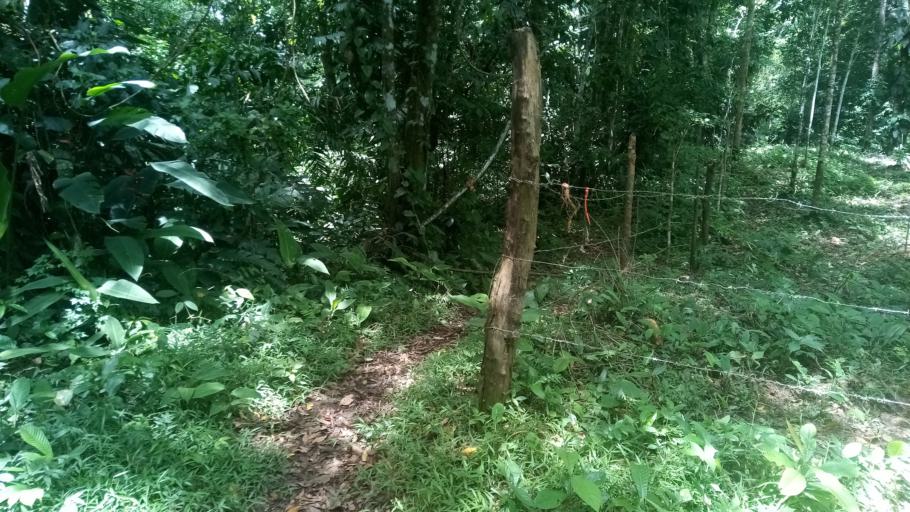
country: CR
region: Limon
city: Sixaola
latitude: 9.6284
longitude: -82.6247
